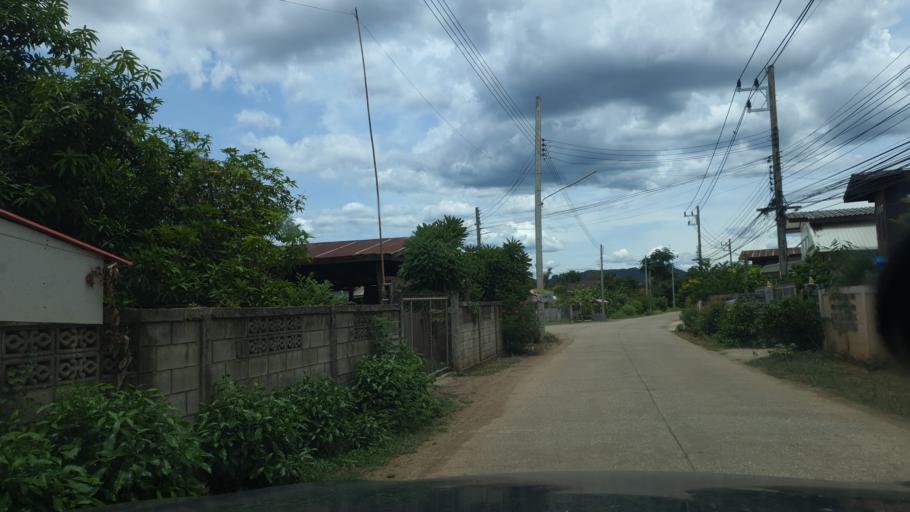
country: TH
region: Sukhothai
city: Thung Saliam
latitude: 17.3134
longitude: 99.5636
